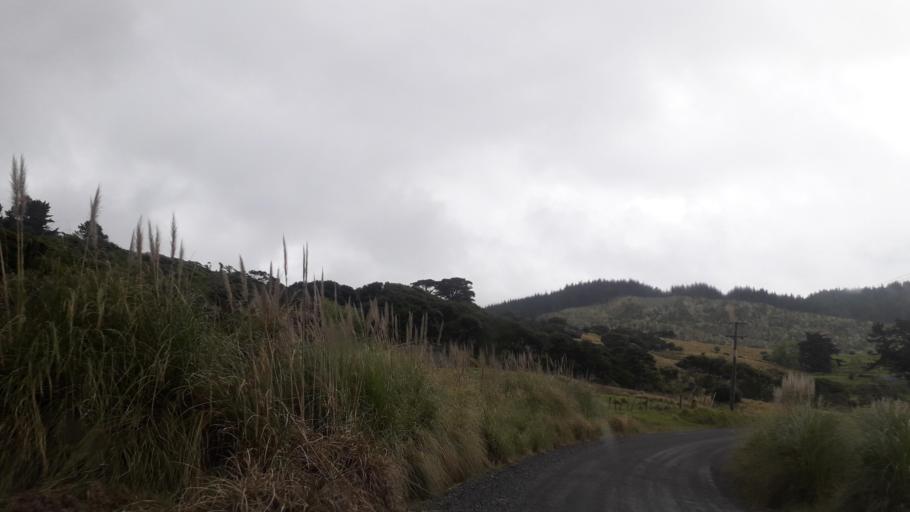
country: NZ
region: Northland
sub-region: Far North District
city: Ahipara
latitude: -35.4360
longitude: 173.3318
